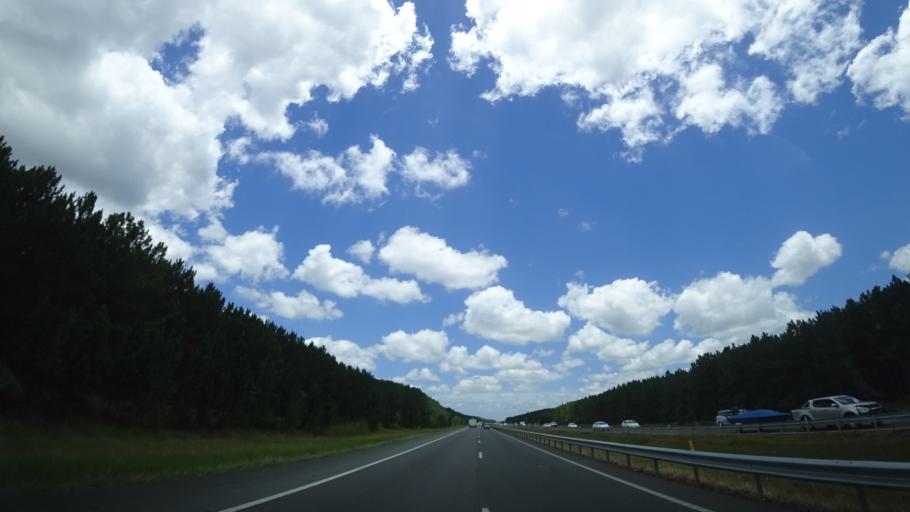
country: AU
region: Queensland
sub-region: Sunshine Coast
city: Little Mountain
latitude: -26.8847
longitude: 153.0064
